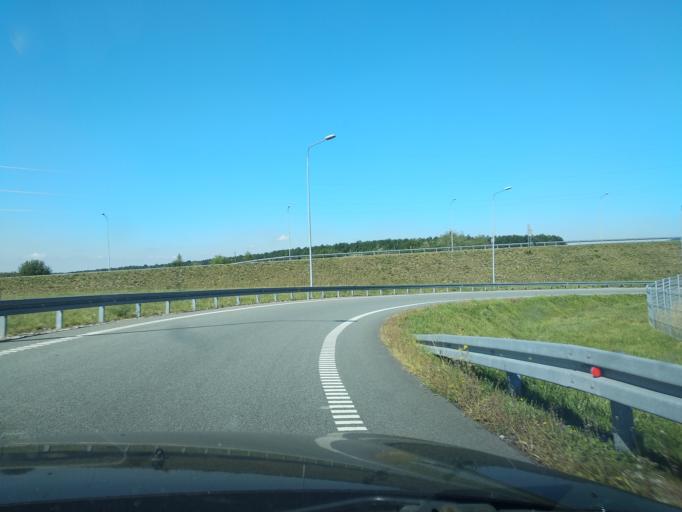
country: PL
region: Swietokrzyskie
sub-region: Powiat kielecki
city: Kostomloty Drugie
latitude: 50.9085
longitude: 20.5779
